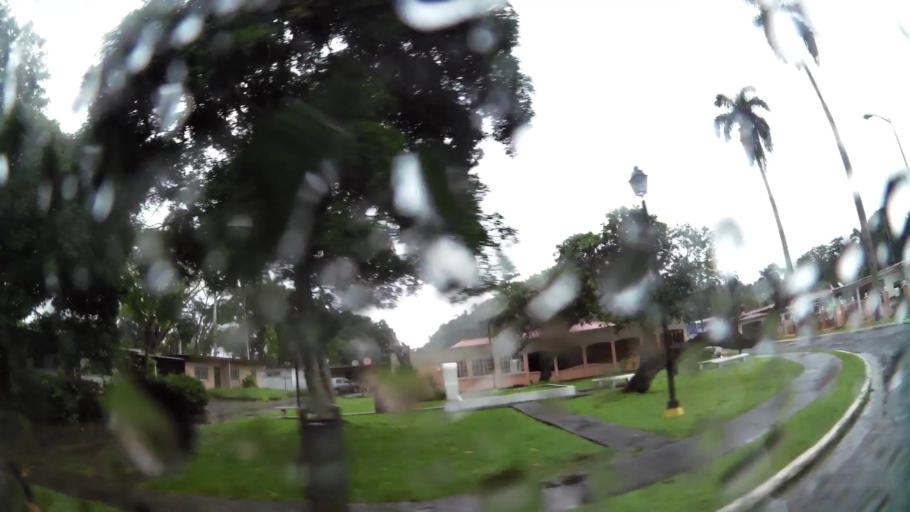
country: PA
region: Panama
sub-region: Distrito de Panama
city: Paraiso
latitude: 9.0186
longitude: -79.6095
